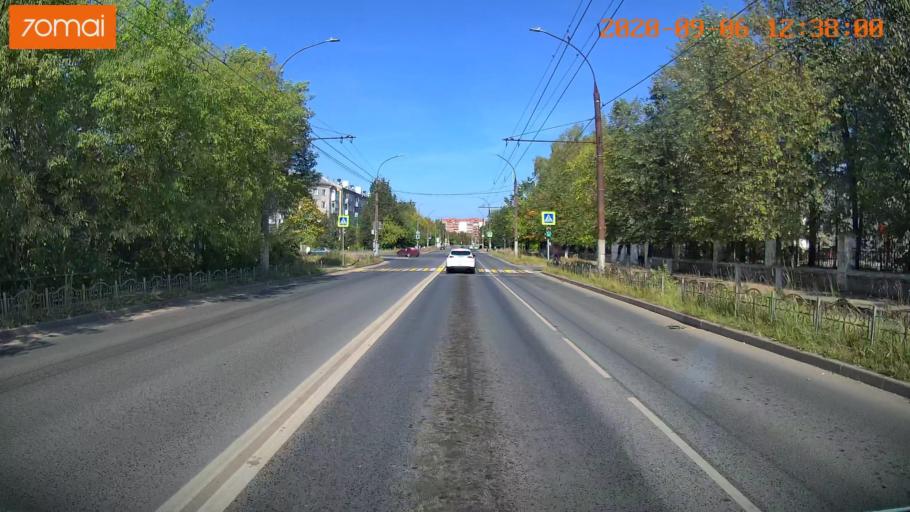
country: RU
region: Ivanovo
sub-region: Gorod Ivanovo
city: Ivanovo
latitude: 57.0298
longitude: 40.9805
